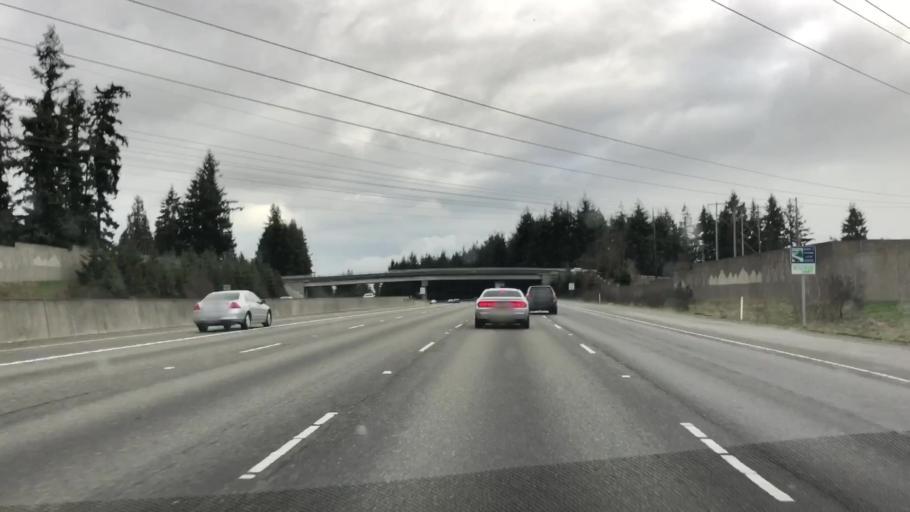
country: US
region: Washington
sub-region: Snohomish County
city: Everett
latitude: 47.9280
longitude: -122.2000
